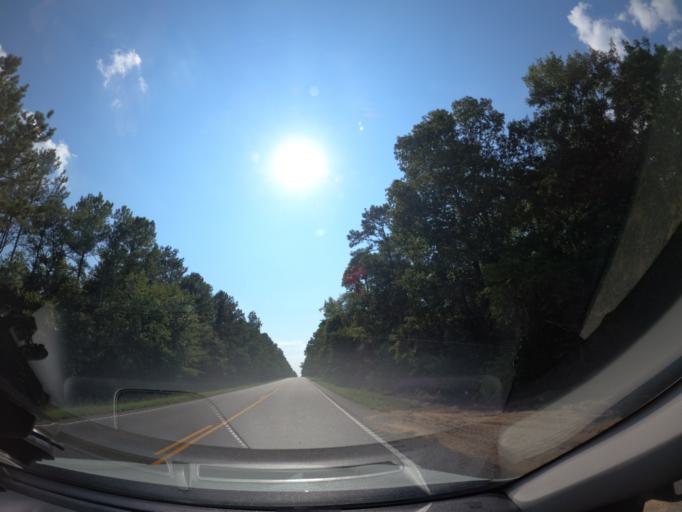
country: US
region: South Carolina
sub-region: Aiken County
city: New Ellenton
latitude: 33.3866
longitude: -81.5996
